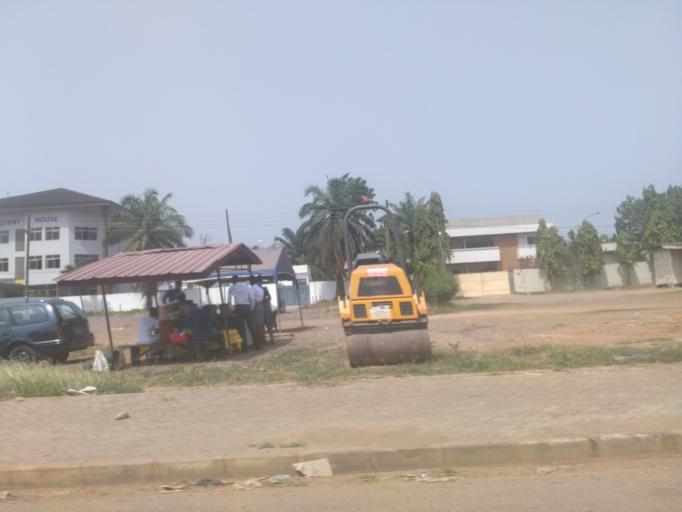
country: GH
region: Greater Accra
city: Dome
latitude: 5.6171
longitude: -0.1987
